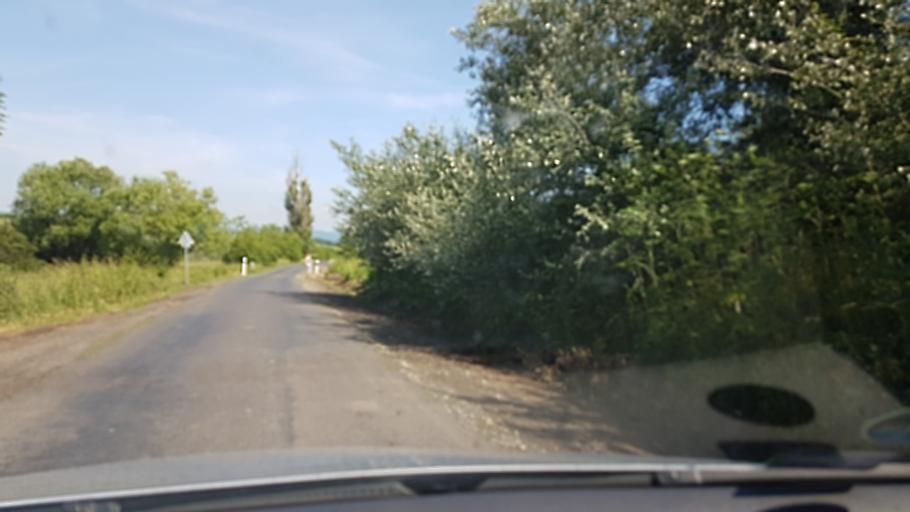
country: HU
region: Borsod-Abauj-Zemplen
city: Saly
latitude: 47.9294
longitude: 20.7132
